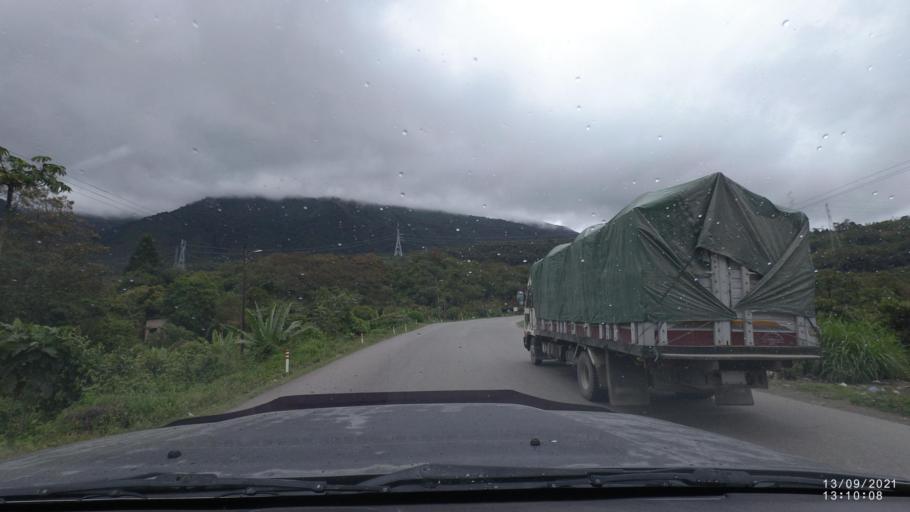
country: BO
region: Cochabamba
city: Colomi
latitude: -17.2090
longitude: -65.8263
